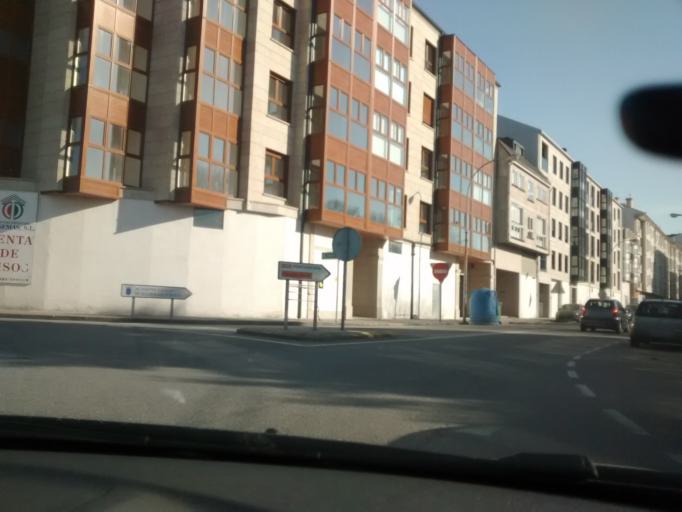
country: ES
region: Galicia
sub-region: Provincia de Pontevedra
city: A Estrada
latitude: 42.6956
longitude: -8.4981
